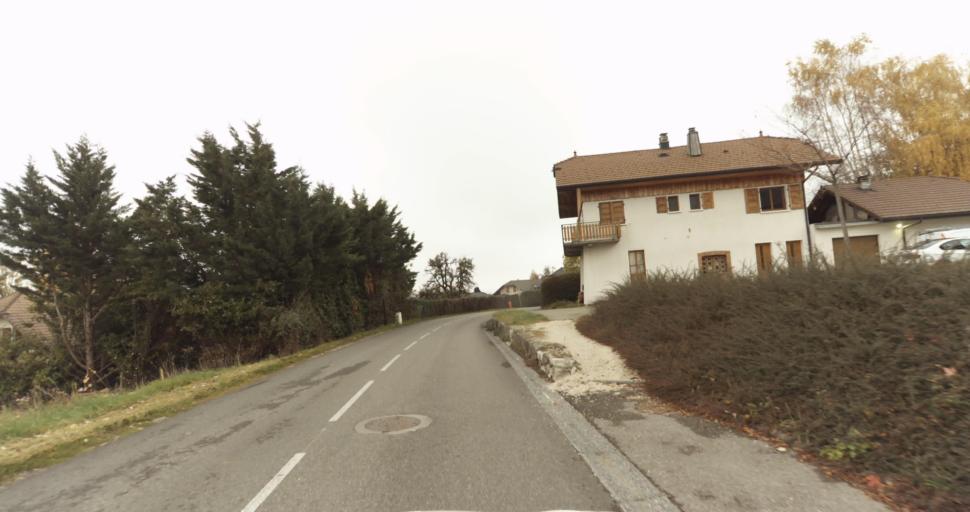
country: FR
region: Rhone-Alpes
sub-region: Departement de la Haute-Savoie
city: Viuz-la-Chiesaz
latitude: 45.8410
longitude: 6.0840
